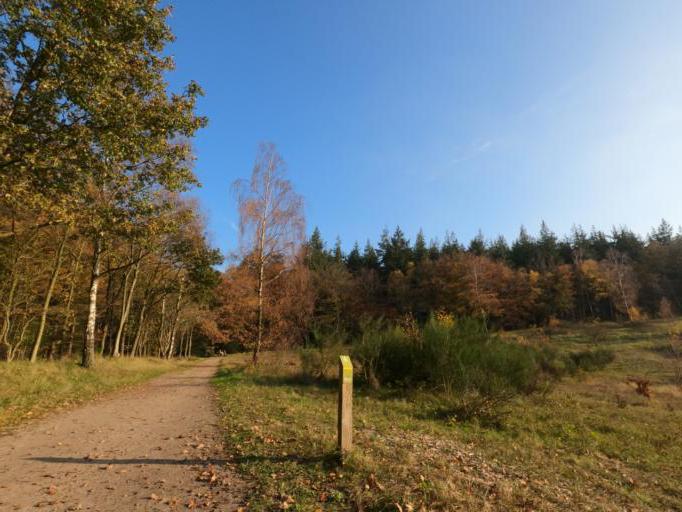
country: NL
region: Utrecht
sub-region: Gemeente Soest
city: Soest
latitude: 52.1365
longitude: 5.2828
